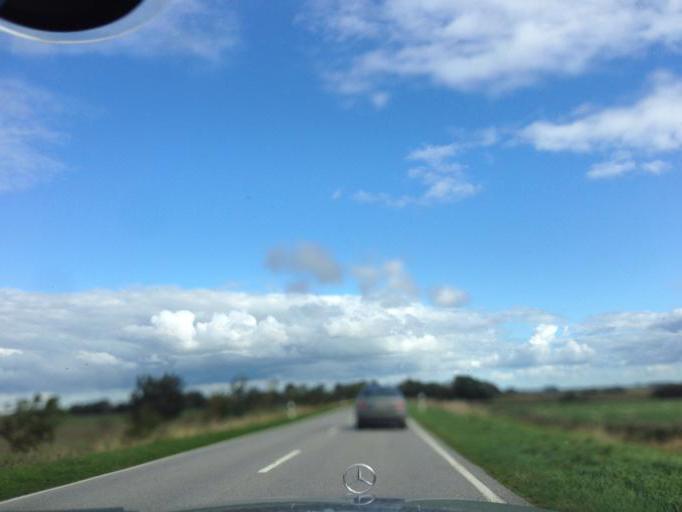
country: DE
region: Schleswig-Holstein
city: Galmsbull
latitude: 54.7742
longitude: 8.7626
